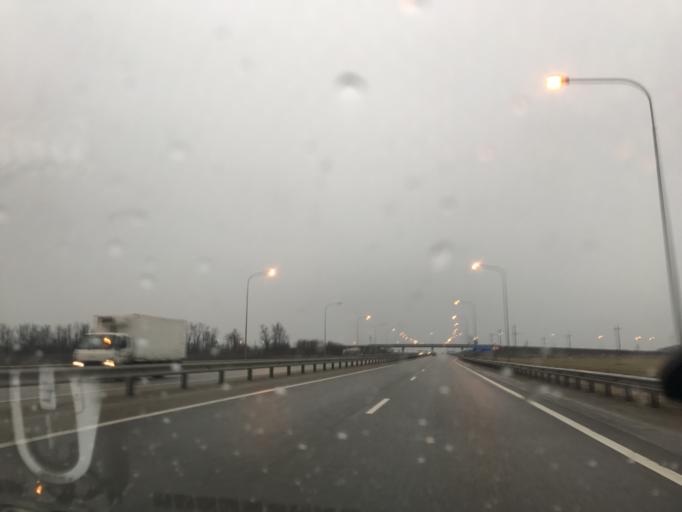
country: RU
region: Krasnodarskiy
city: Pavlovskaya
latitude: 46.2483
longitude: 39.8316
